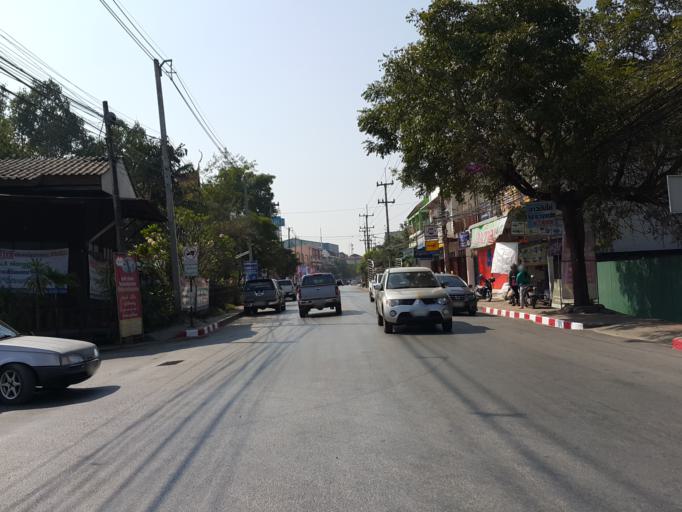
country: TH
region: Lamphun
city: Lamphun
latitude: 18.5953
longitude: 99.0155
